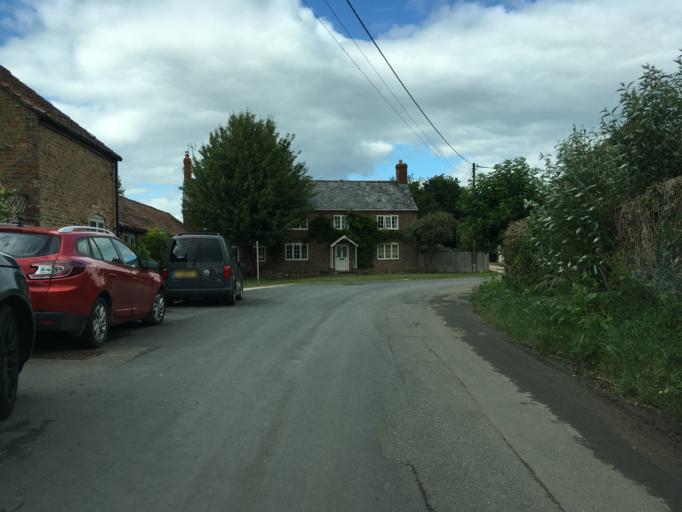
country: GB
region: England
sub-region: Gloucestershire
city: Cinderford
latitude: 51.7985
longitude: -2.4236
